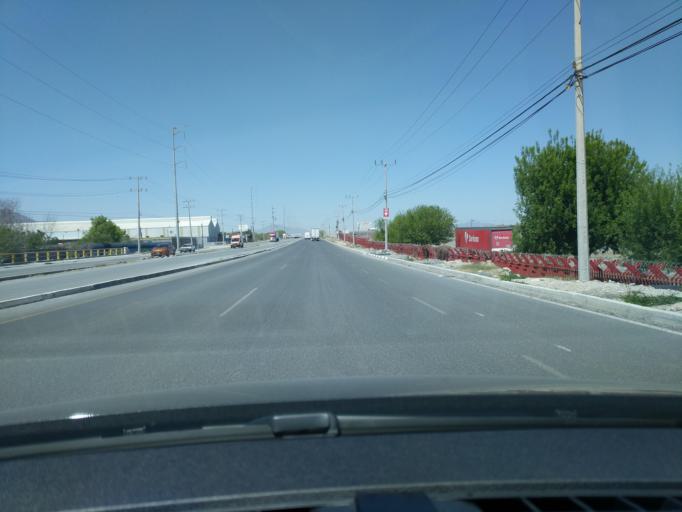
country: MX
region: Nuevo Leon
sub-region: Salinas Victoria
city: Emiliano Zapata
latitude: 25.8959
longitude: -100.2607
